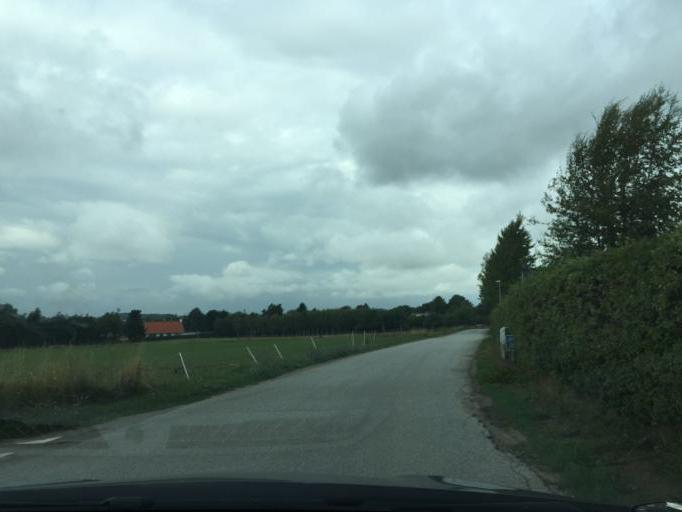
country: DK
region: South Denmark
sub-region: Assens Kommune
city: Harby
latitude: 55.1986
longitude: 10.1203
